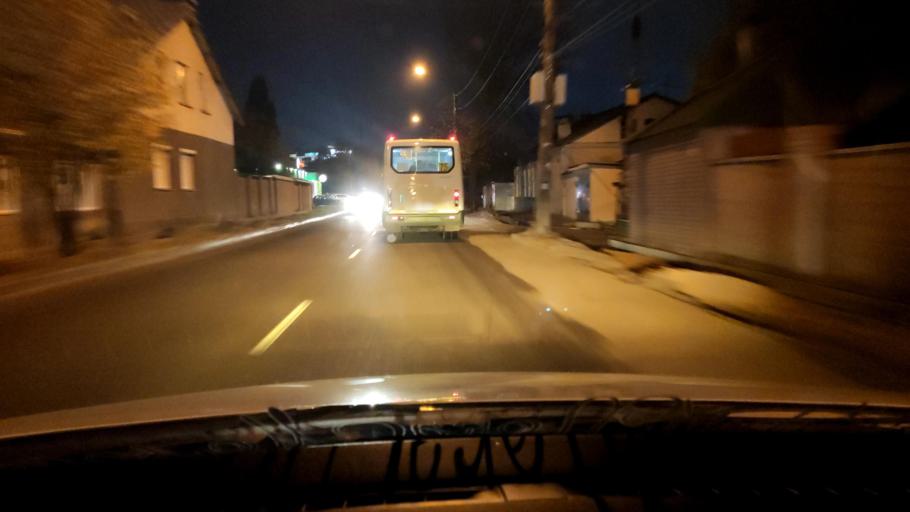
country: RU
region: Voronezj
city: Voronezh
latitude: 51.6873
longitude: 39.2108
